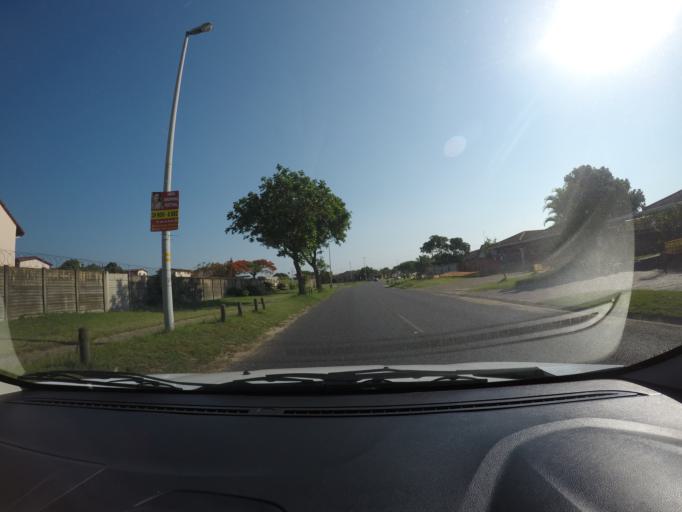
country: ZA
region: KwaZulu-Natal
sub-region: uThungulu District Municipality
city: Richards Bay
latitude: -28.7296
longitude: 32.0415
